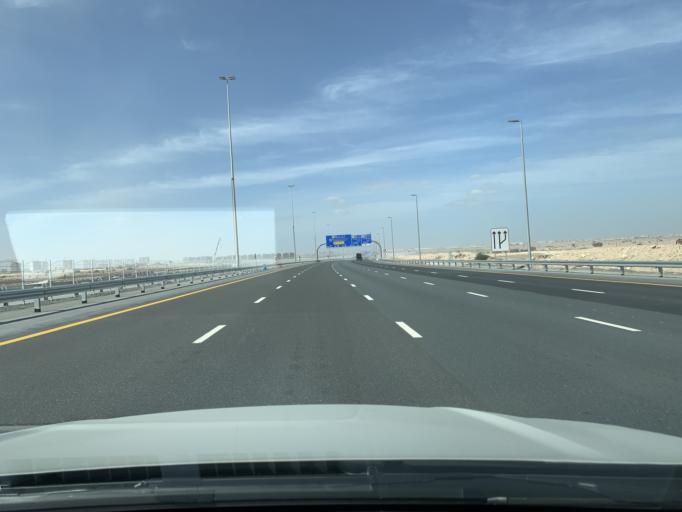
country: AE
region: Dubai
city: Dubai
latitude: 24.9508
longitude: 55.2506
